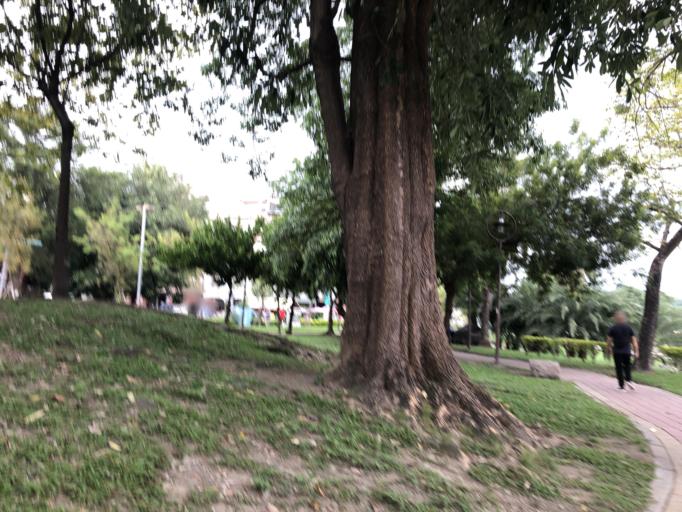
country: TW
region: Kaohsiung
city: Kaohsiung
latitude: 22.6827
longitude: 120.2932
